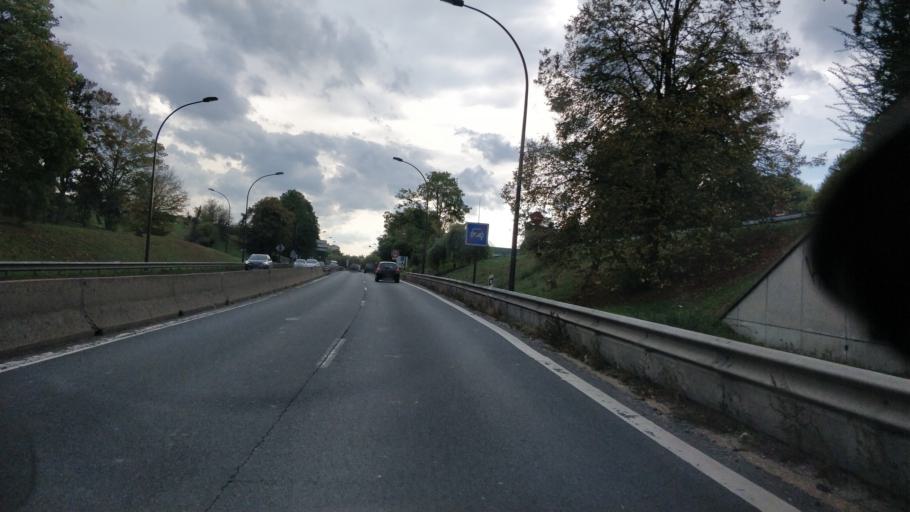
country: FR
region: Ile-de-France
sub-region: Departement de Seine-Saint-Denis
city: Livry-Gargan
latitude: 48.9296
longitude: 2.5534
